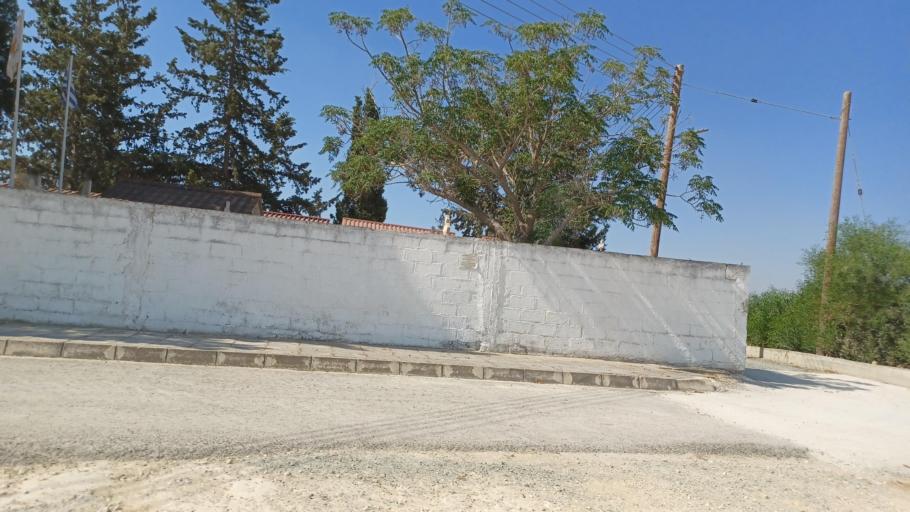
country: CY
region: Ammochostos
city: Acheritou
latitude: 35.0721
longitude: 33.8732
